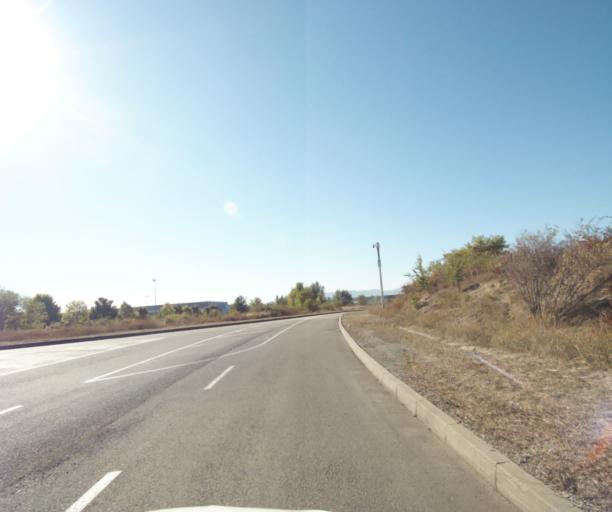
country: FR
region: Auvergne
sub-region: Departement du Puy-de-Dome
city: Gerzat
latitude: 45.8345
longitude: 3.1291
